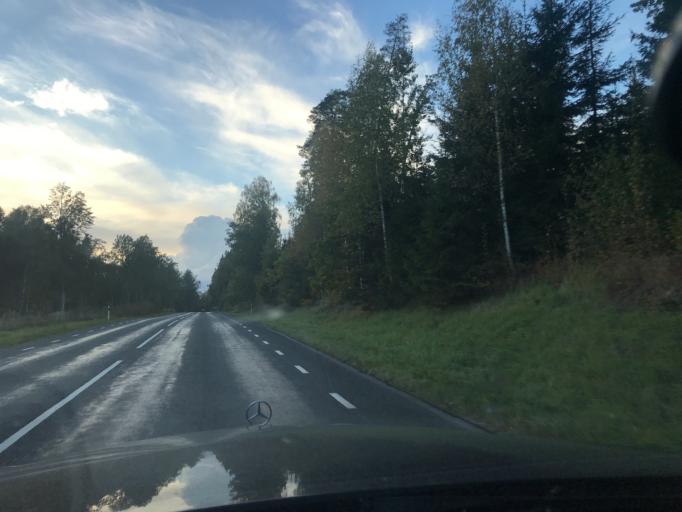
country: EE
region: Vorumaa
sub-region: Antsla vald
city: Vana-Antsla
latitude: 57.8812
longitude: 26.5737
